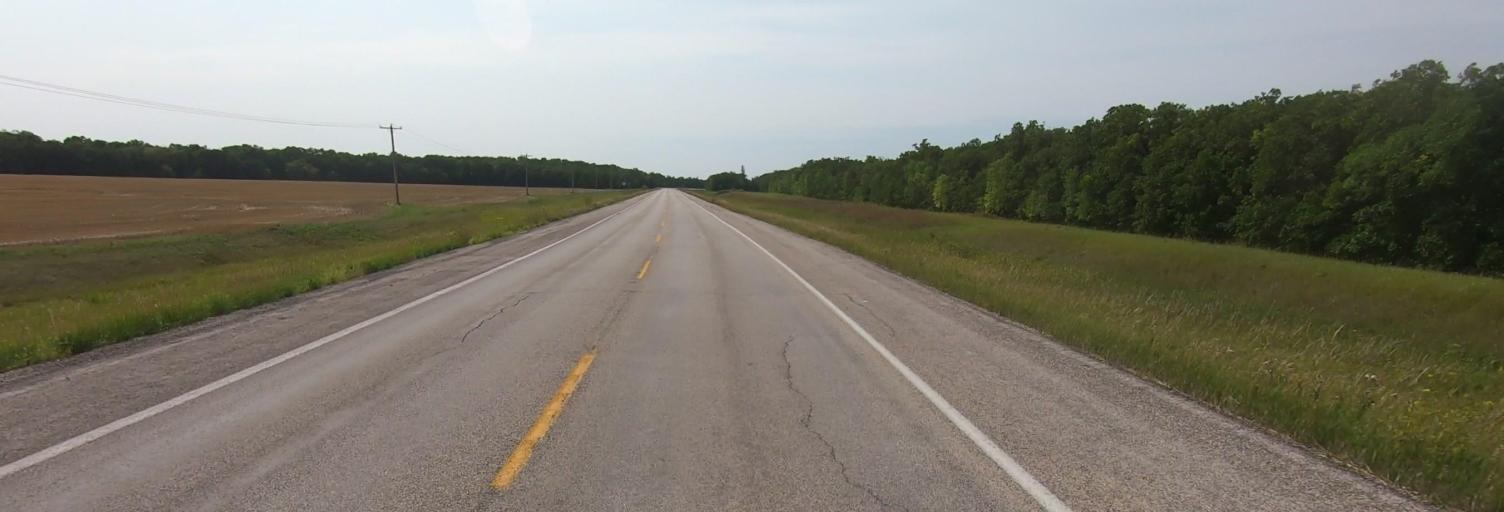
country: CA
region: Manitoba
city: Niverville
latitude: 49.5957
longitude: -97.1348
